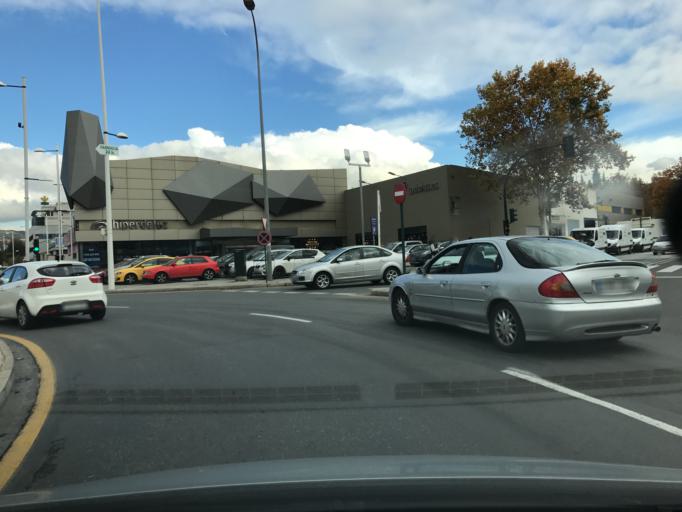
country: ES
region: Andalusia
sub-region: Provincia de Granada
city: Armilla
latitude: 37.1582
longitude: -3.6071
